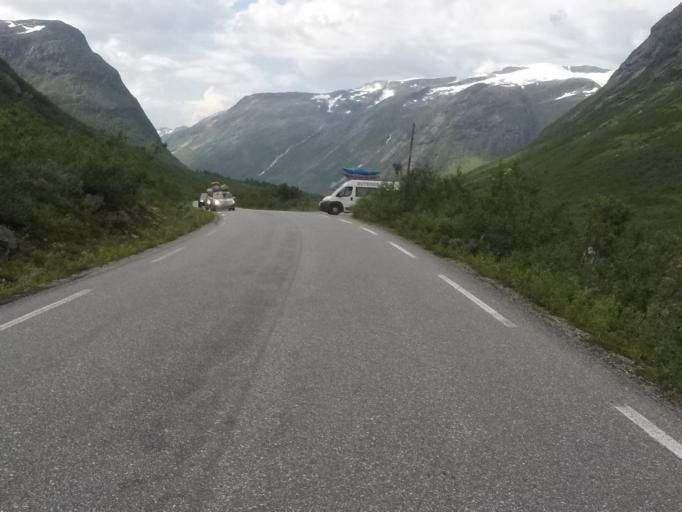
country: NO
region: More og Romsdal
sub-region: Rauma
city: Andalsnes
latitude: 62.3952
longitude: 7.5997
